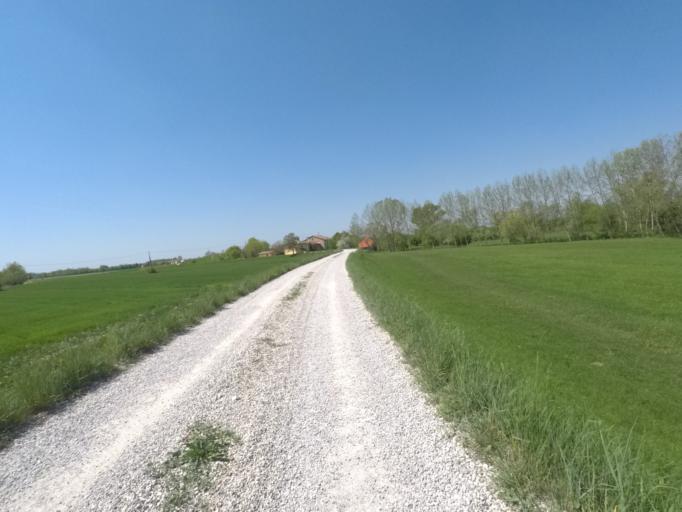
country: IT
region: Veneto
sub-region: Provincia di Treviso
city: Mansue
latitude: 45.8249
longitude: 12.5604
